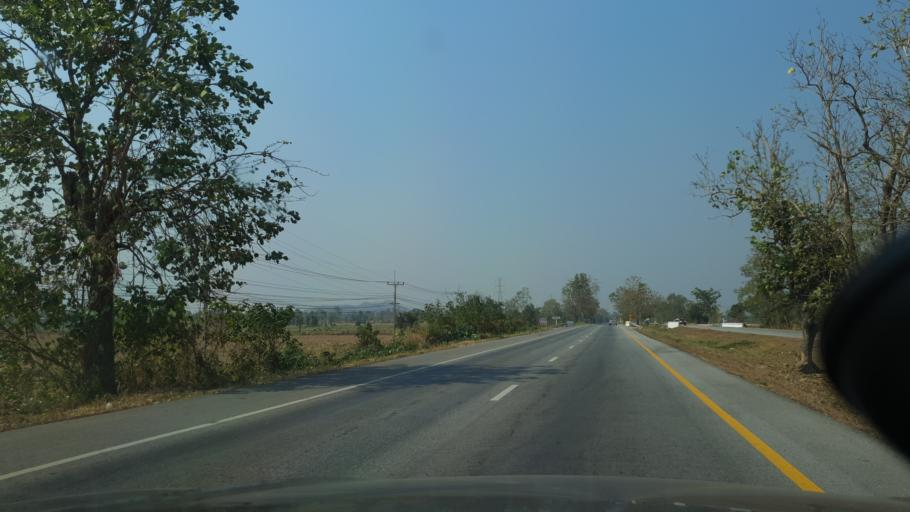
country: TH
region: Kamphaeng Phet
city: Kosamphi Nakhon
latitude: 16.6338
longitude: 99.3434
